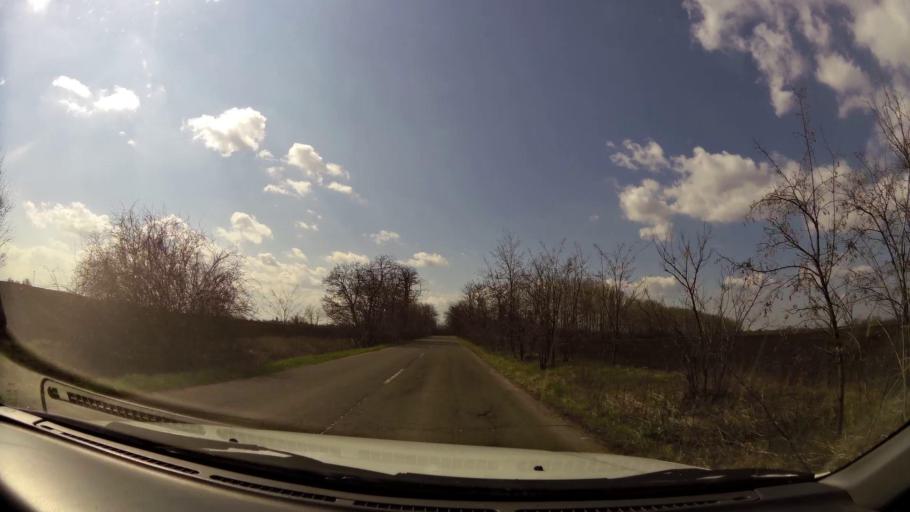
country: HU
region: Pest
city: Tapioszele
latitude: 47.3351
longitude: 19.8972
